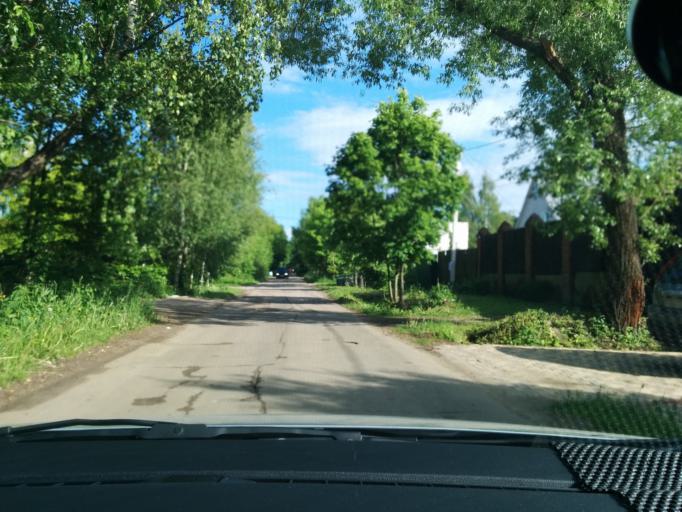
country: RU
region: Moskovskaya
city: Lugovaya
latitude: 56.0535
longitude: 37.4857
